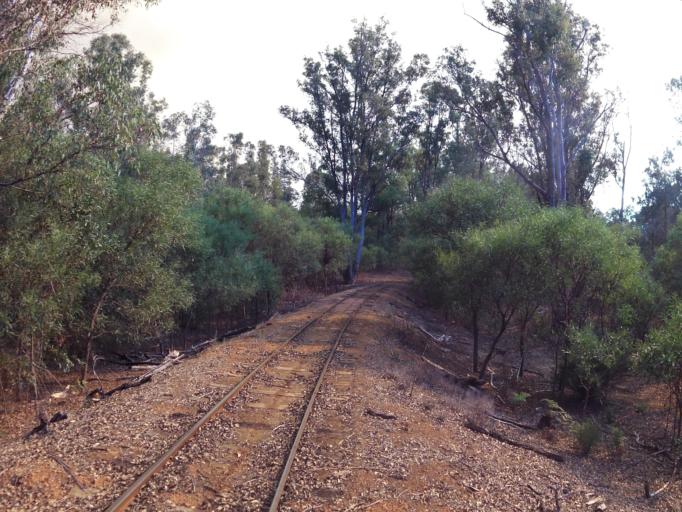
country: AU
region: Western Australia
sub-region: Waroona
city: Waroona
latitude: -32.7386
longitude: 116.1296
